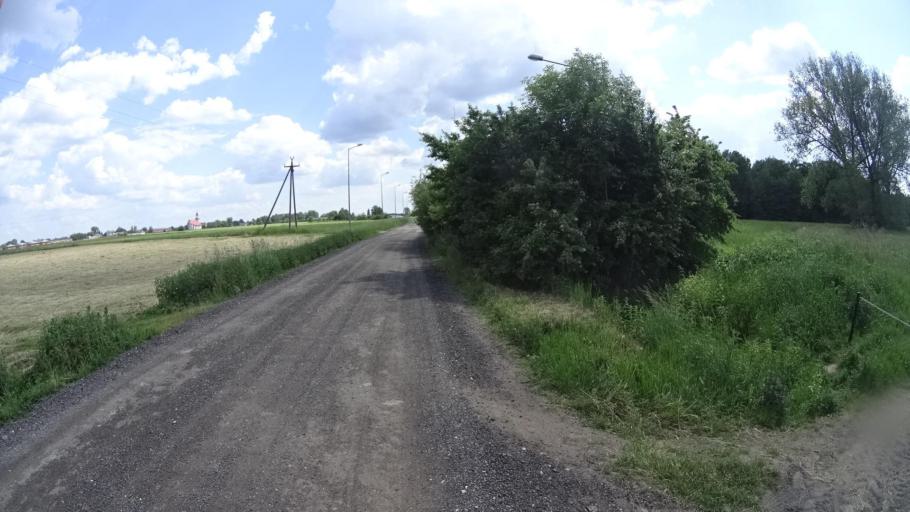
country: PL
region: Masovian Voivodeship
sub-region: Powiat pruszkowski
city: Nadarzyn
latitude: 52.0604
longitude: 20.8225
